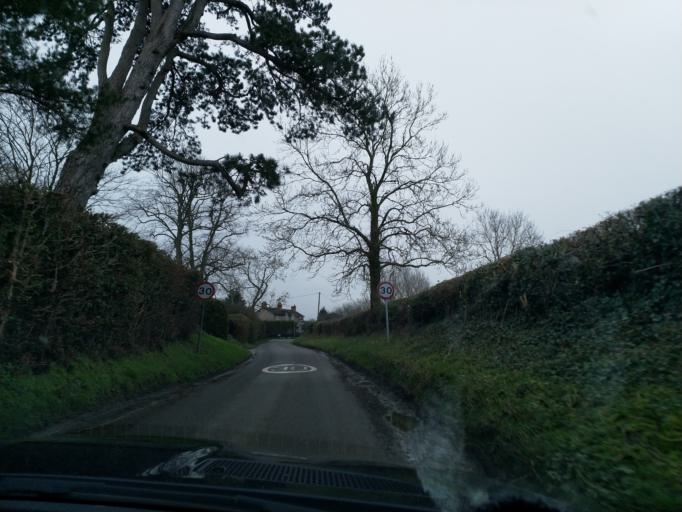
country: GB
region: England
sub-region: Northamptonshire
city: Brackley
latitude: 52.0527
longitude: -1.2240
